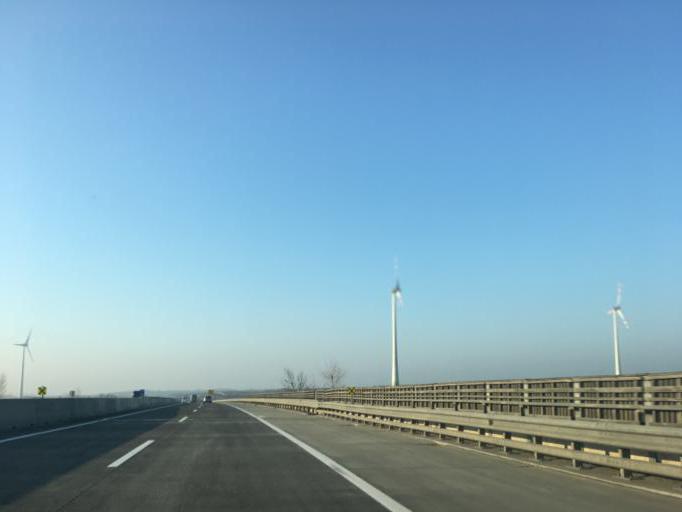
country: AT
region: Burgenland
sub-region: Politischer Bezirk Neusiedl am See
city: Gattendorf
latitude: 48.0511
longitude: 16.9955
